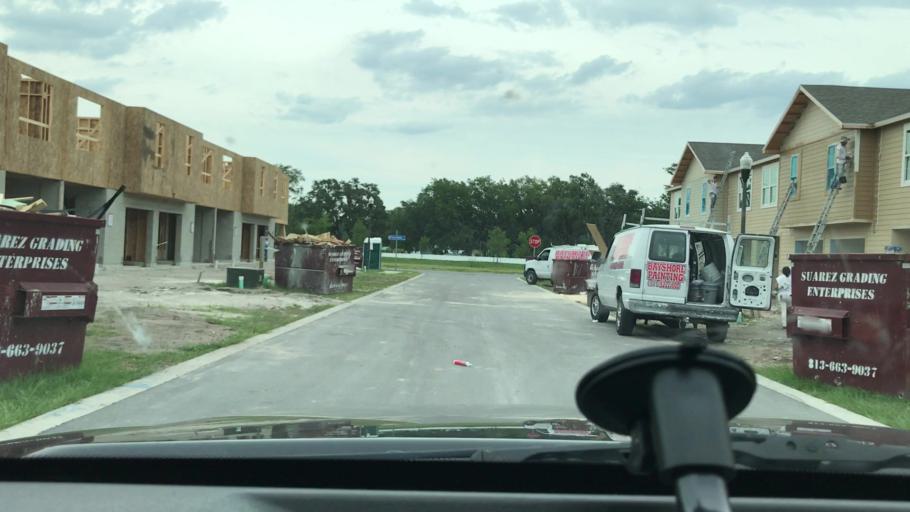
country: US
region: Florida
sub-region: Hillsborough County
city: Riverview
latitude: 27.8596
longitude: -82.3309
